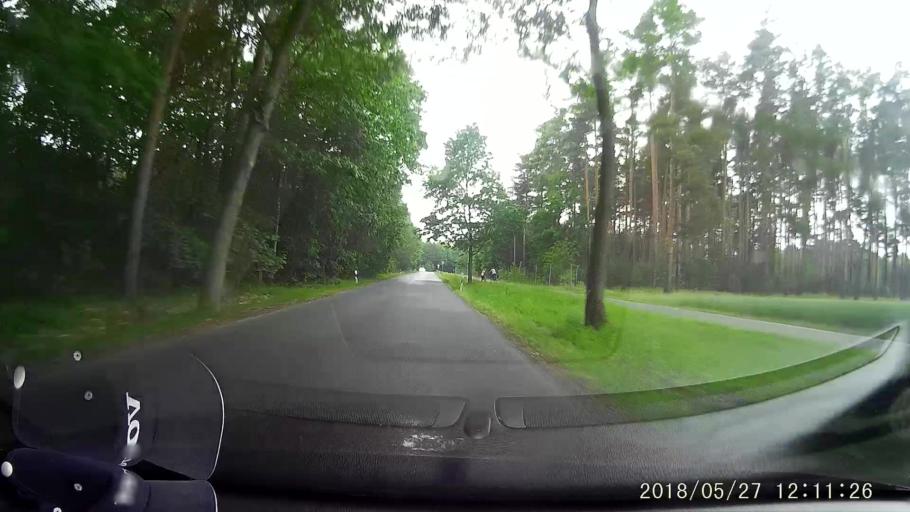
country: DE
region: Saxony
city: Klitten
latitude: 51.3578
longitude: 14.5730
